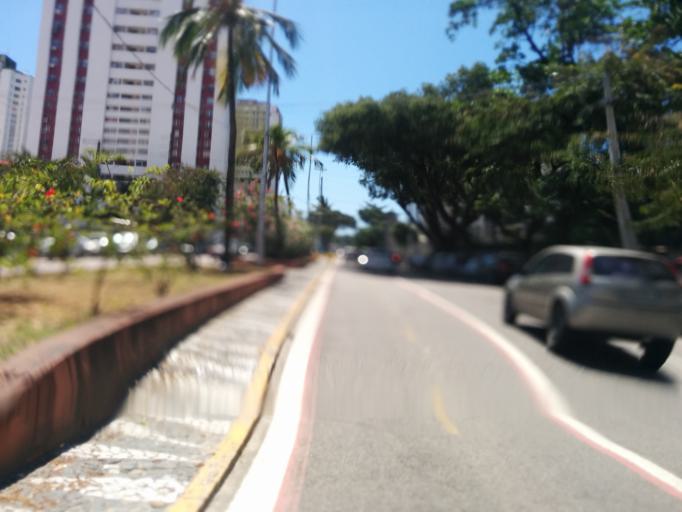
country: BR
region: Pernambuco
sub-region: Recife
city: Recife
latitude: -8.0552
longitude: -34.8798
